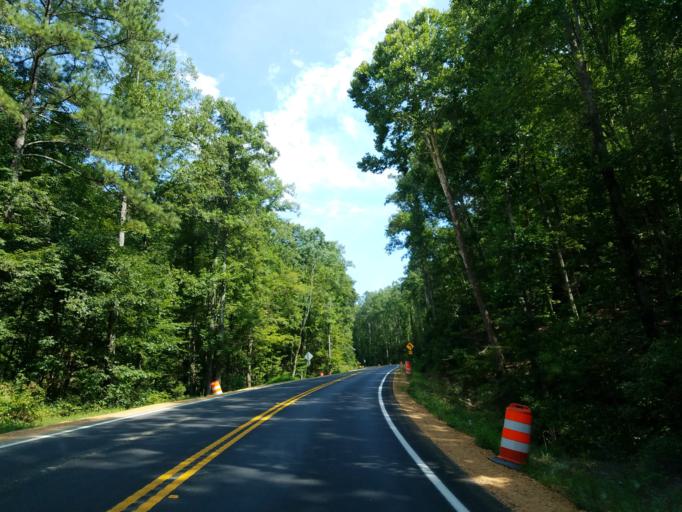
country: US
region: Georgia
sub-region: Gilmer County
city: Ellijay
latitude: 34.5811
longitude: -84.6408
